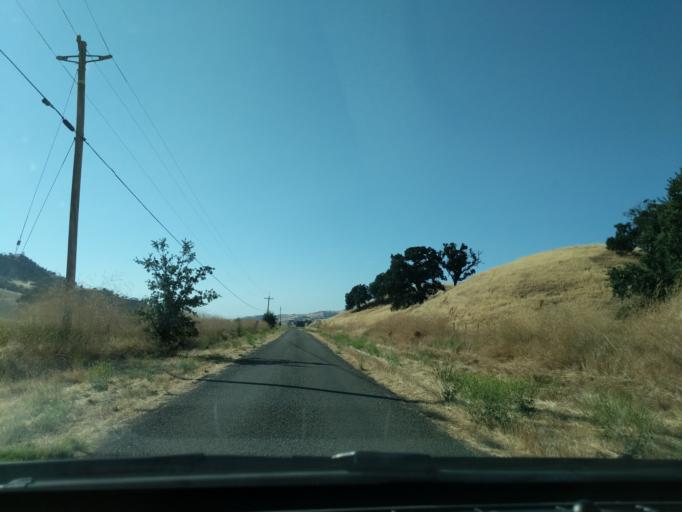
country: US
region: California
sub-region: Monterey County
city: King City
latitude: 36.1395
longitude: -120.7511
